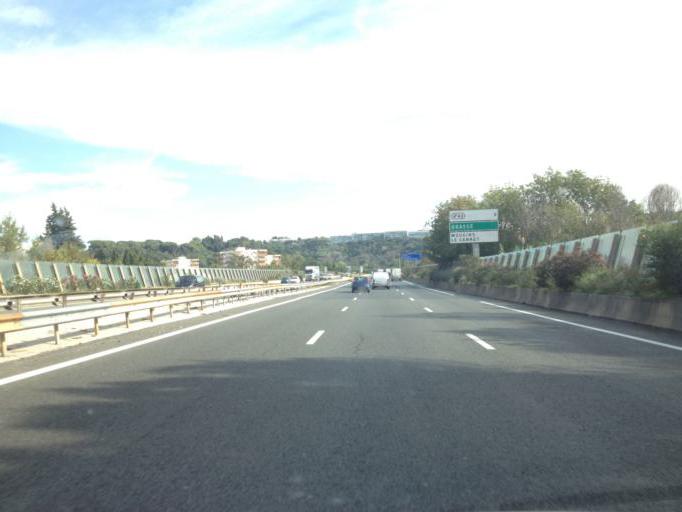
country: FR
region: Provence-Alpes-Cote d'Azur
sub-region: Departement des Alpes-Maritimes
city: Mandelieu-la-Napoule
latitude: 43.5591
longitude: 6.9643
